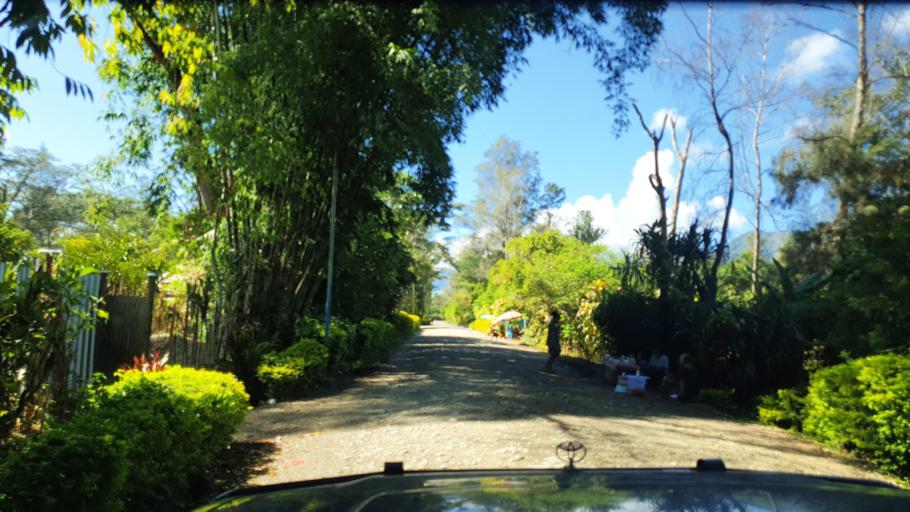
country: PG
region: Western Highlands
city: Rauna
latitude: -5.8208
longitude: 144.3844
